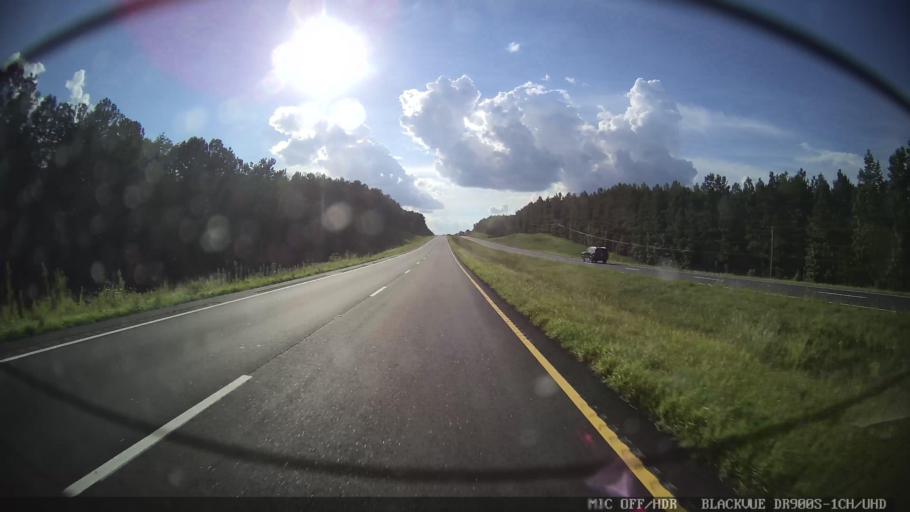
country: US
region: Georgia
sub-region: Floyd County
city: Lindale
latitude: 34.2108
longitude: -85.0966
